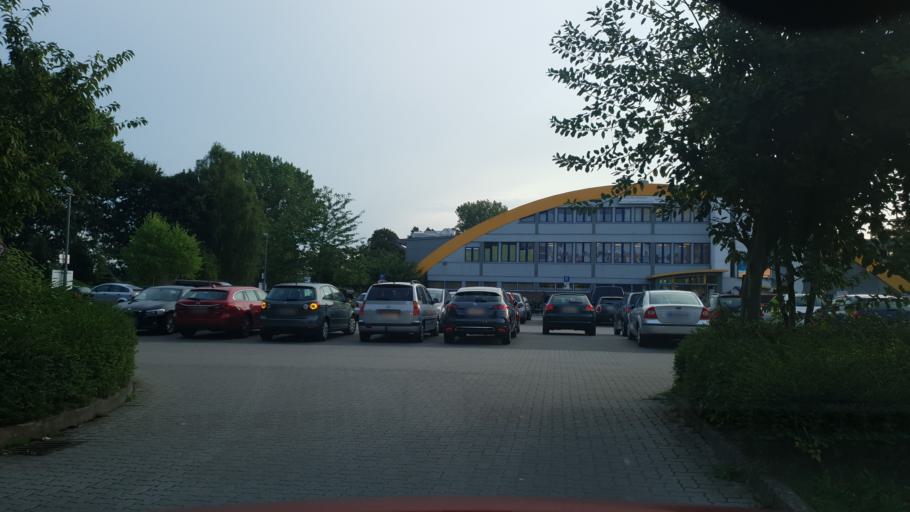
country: DE
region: Schleswig-Holstein
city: Kronshagen
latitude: 54.3427
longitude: 10.1118
